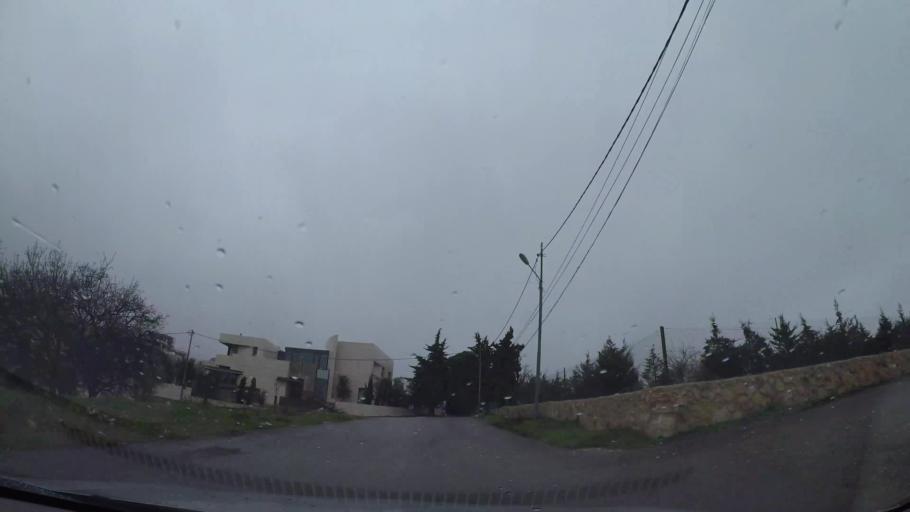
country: JO
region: Amman
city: Wadi as Sir
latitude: 32.0046
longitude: 35.7998
